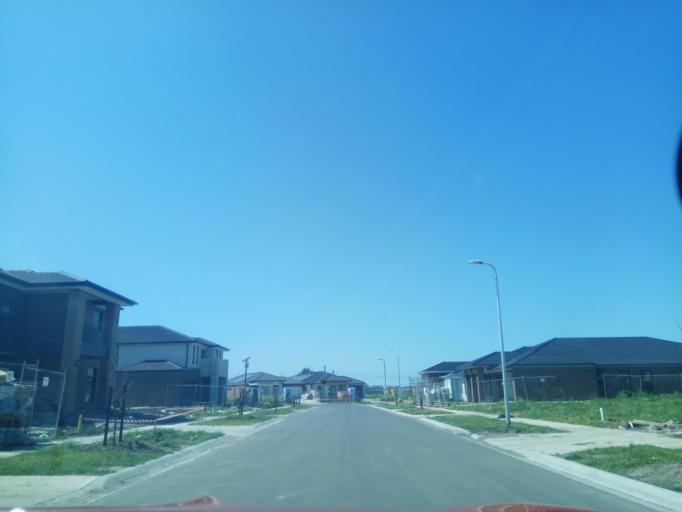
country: AU
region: Victoria
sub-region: Casey
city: Lynbrook
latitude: -38.0645
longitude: 145.2510
